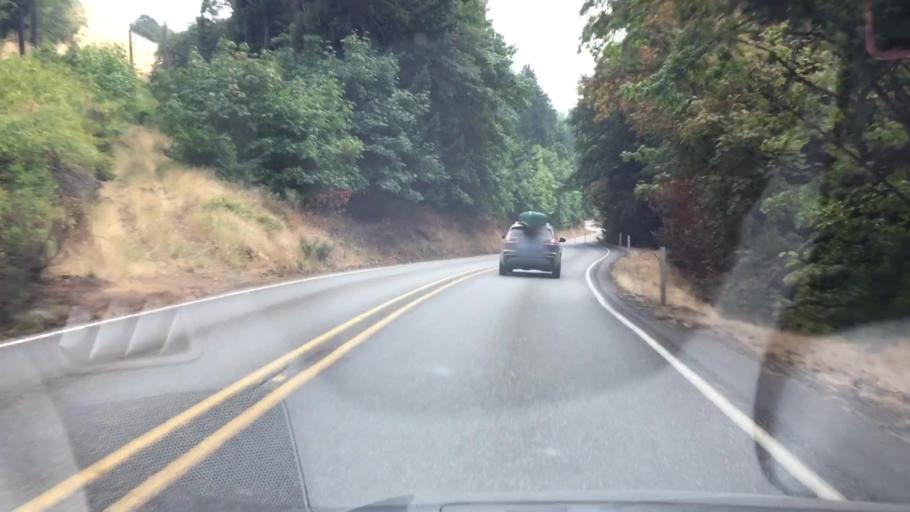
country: US
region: Washington
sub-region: Klickitat County
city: White Salmon
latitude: 45.7511
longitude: -121.5176
